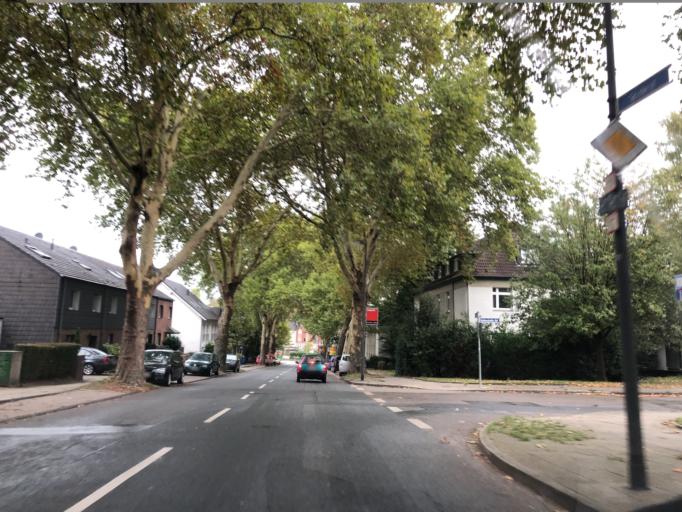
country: DE
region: North Rhine-Westphalia
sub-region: Regierungsbezirk Dusseldorf
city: Essen
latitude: 51.4661
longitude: 7.0636
